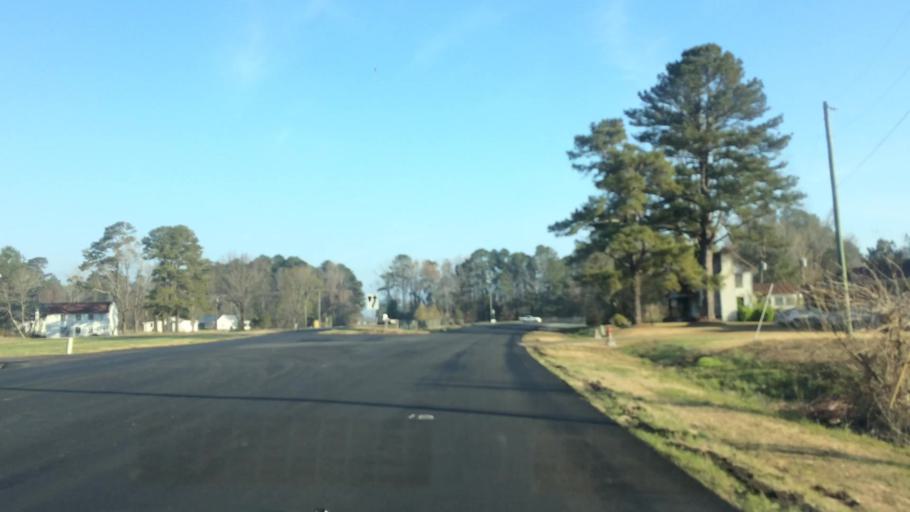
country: US
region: North Carolina
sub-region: Pitt County
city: Farmville
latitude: 35.6824
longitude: -77.6435
